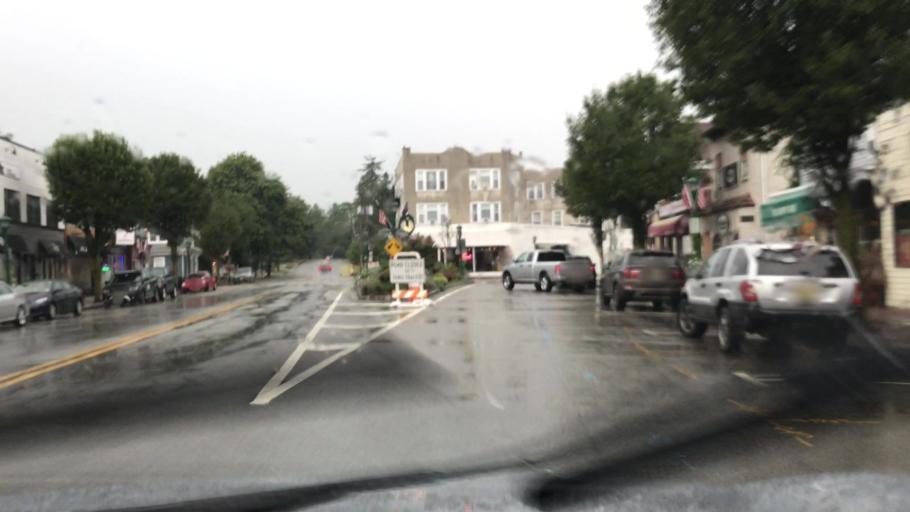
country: US
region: New Jersey
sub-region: Bergen County
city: Closter
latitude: 40.9734
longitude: -73.9619
